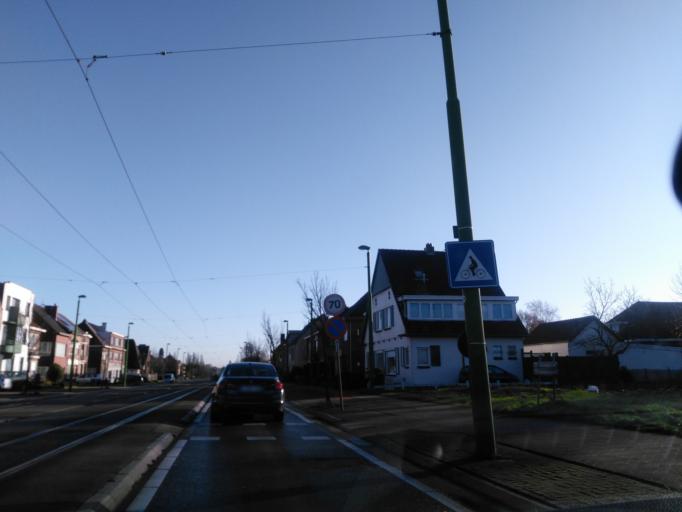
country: BE
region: Flanders
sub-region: Provincie Antwerpen
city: Zwijndrecht
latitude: 51.2193
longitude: 4.3108
